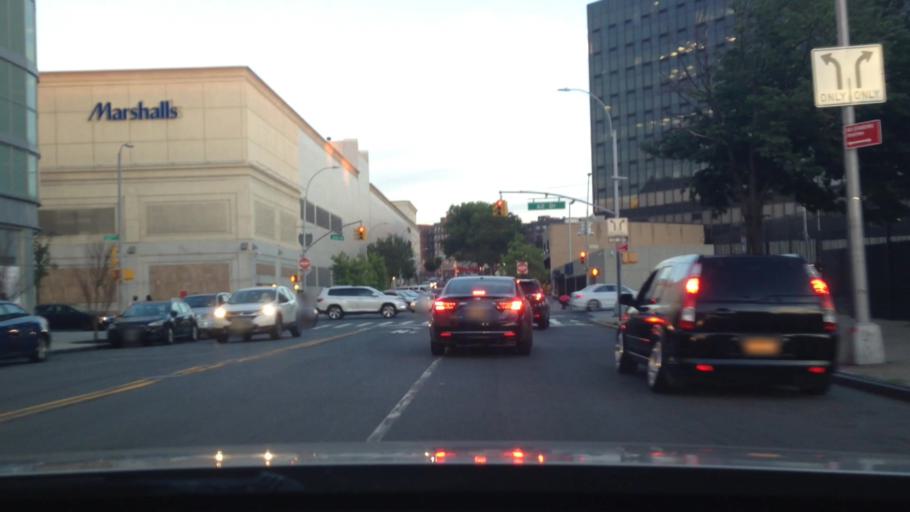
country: US
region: New York
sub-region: Queens County
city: Borough of Queens
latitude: 40.7325
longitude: -73.8637
